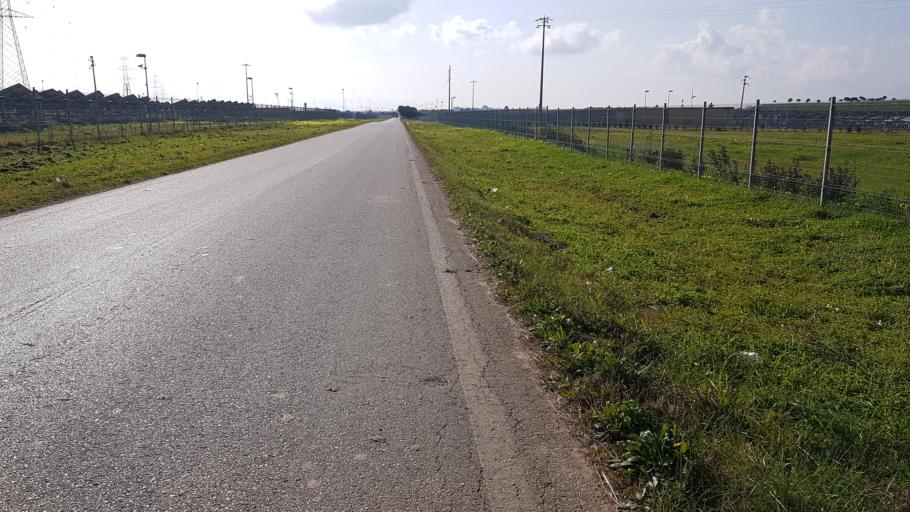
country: IT
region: Apulia
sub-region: Provincia di Brindisi
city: La Rosa
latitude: 40.5897
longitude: 17.9030
